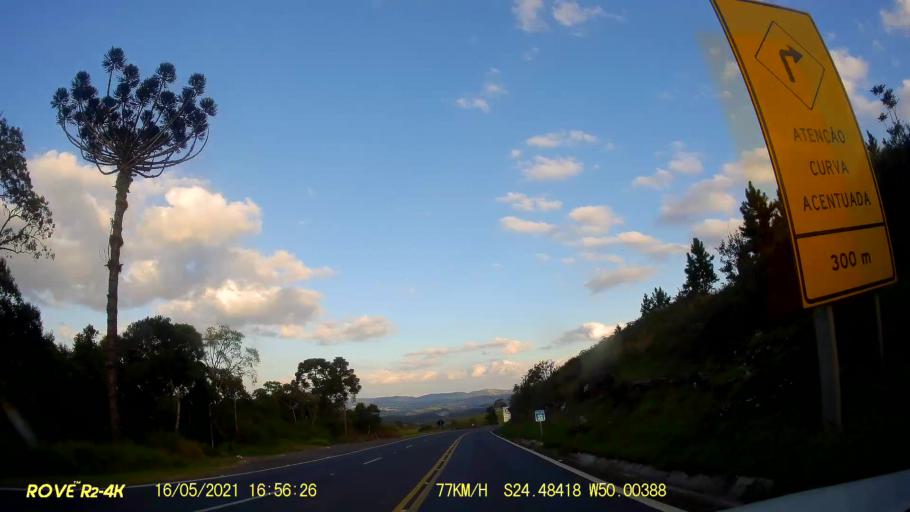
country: BR
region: Parana
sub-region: Pirai Do Sul
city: Pirai do Sul
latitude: -24.4843
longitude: -50.0035
